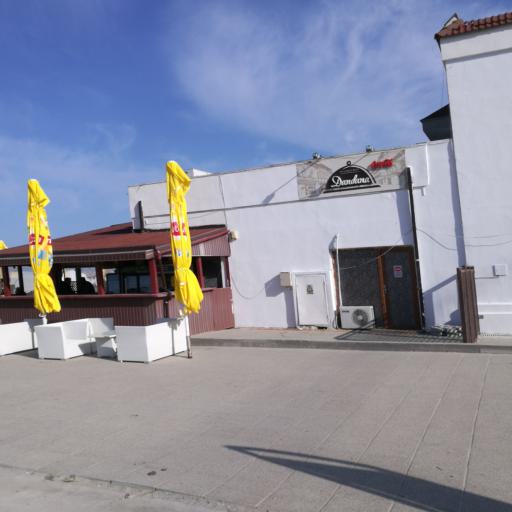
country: RO
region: Constanta
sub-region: Municipiul Constanta
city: Palazu Mare
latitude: 44.2350
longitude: 28.6263
